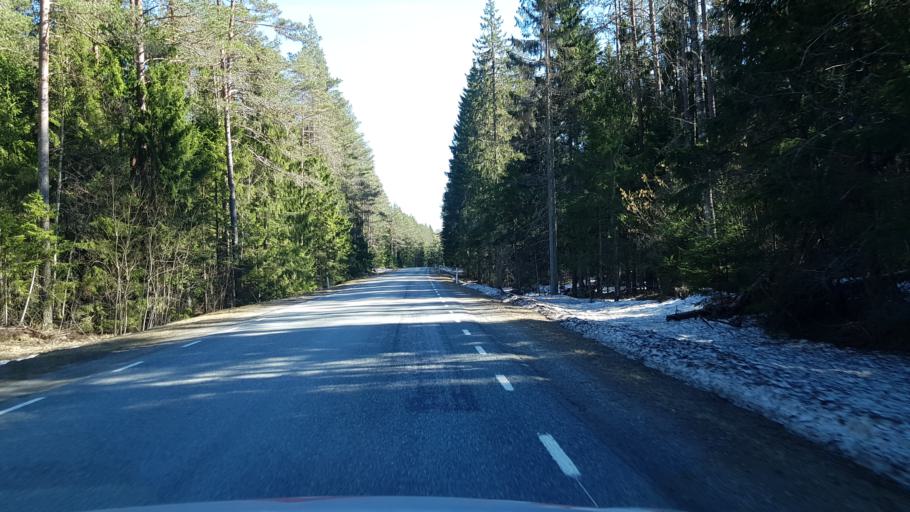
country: EE
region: Laeaene-Virumaa
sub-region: Vinni vald
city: Vinni
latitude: 59.2600
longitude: 26.6826
